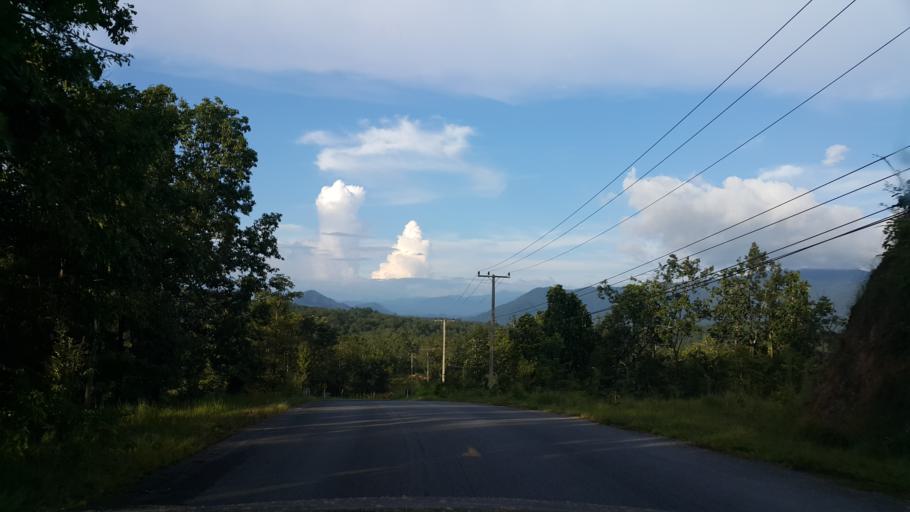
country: TH
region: Mae Hong Son
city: Mae Hi
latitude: 19.1778
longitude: 98.3969
